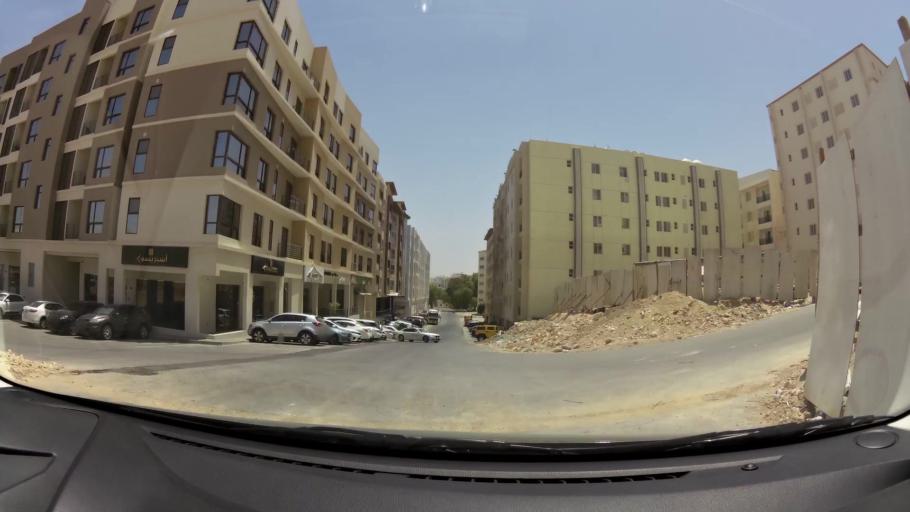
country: OM
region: Muhafazat Masqat
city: Muscat
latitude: 23.6217
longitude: 58.5025
